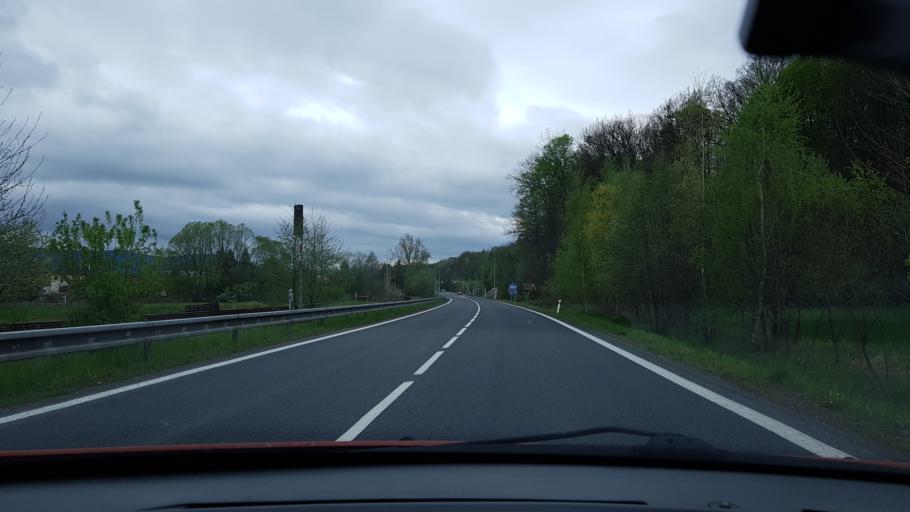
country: CZ
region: Olomoucky
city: Mikulovice
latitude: 50.3053
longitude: 17.3256
